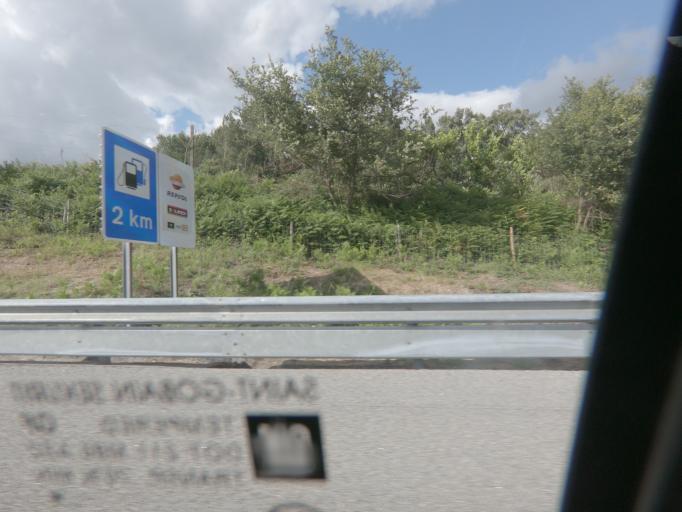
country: PT
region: Porto
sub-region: Marco de Canaveses
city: Marco de Canavezes
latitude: 41.2204
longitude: -8.1579
